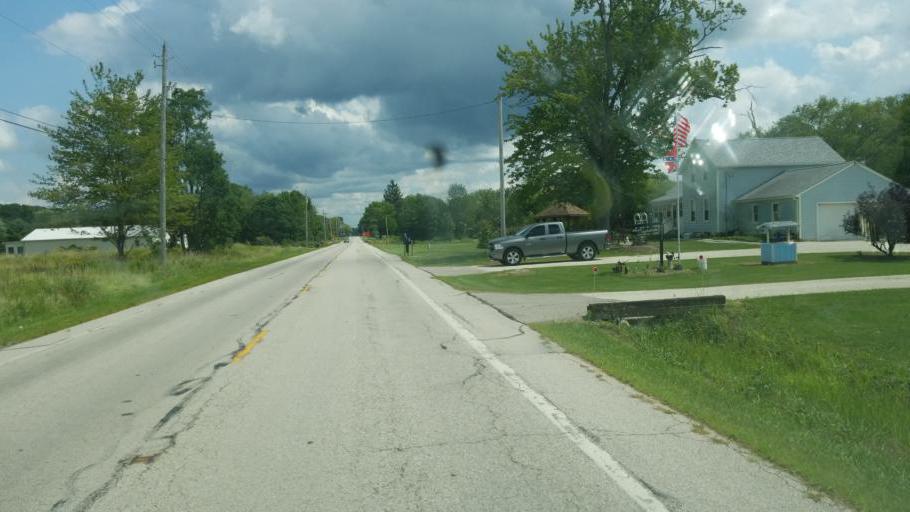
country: US
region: Ohio
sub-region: Ashtabula County
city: Andover
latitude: 41.6069
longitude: -80.6737
